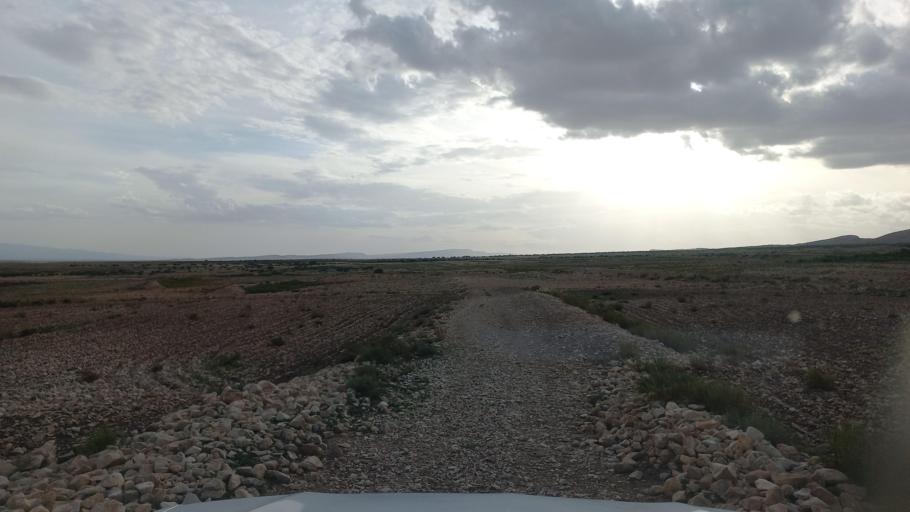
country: TN
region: Al Qasrayn
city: Sbiba
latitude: 35.4480
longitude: 9.0631
